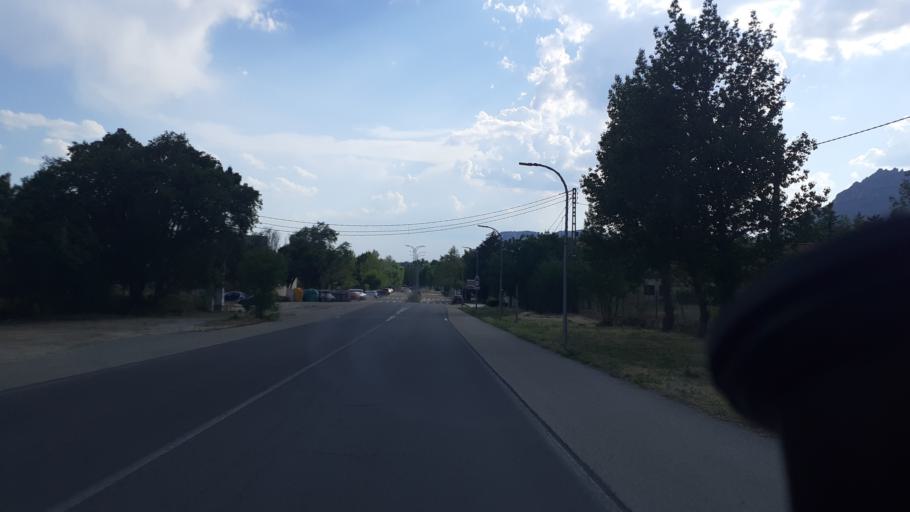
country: ES
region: Madrid
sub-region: Provincia de Madrid
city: La Cabrera
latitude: 40.8742
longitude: -3.6048
